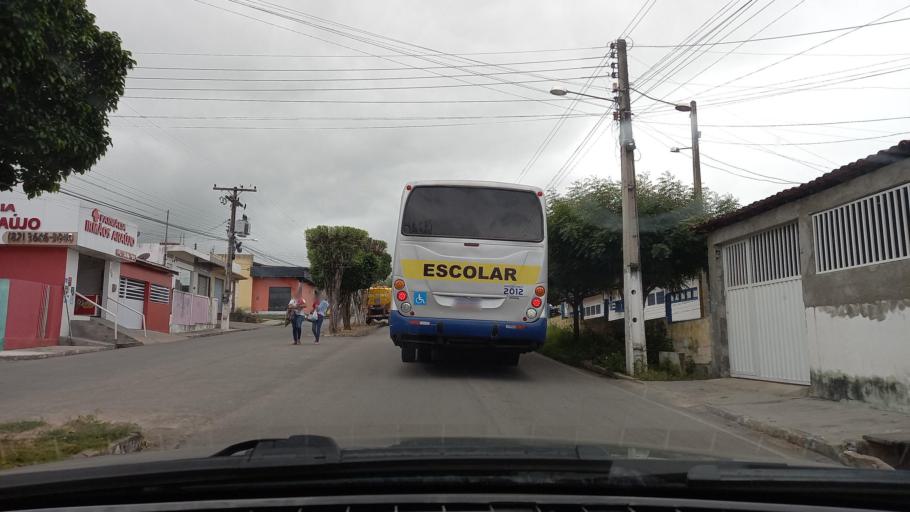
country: BR
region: Sergipe
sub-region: Caninde De Sao Francisco
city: Caninde de Sao Francisco
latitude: -9.6057
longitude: -37.7587
